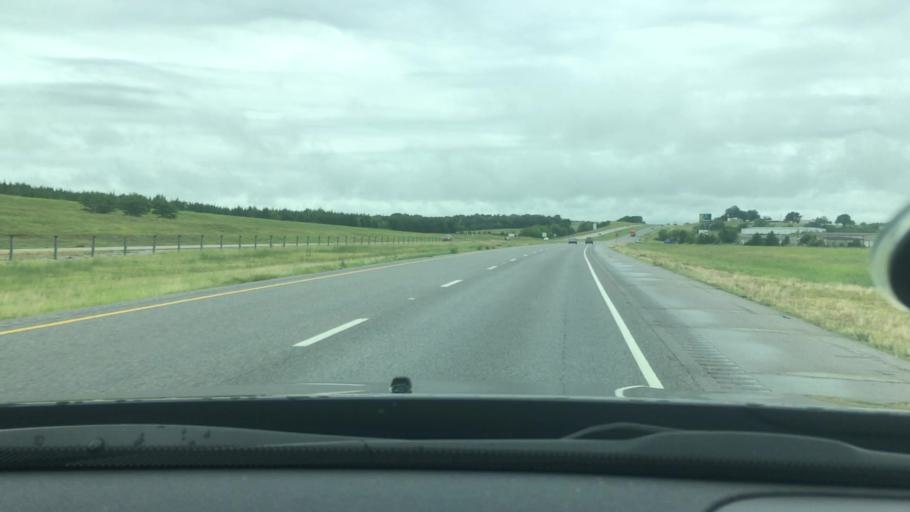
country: US
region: Oklahoma
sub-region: Bryan County
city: Durant
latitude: 34.1322
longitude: -96.2744
